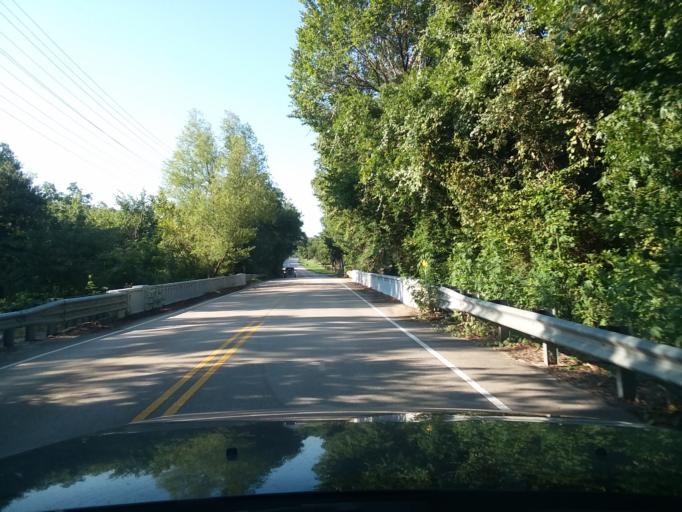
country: US
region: Texas
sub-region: Denton County
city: Copper Canyon
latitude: 33.1048
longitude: -97.0877
